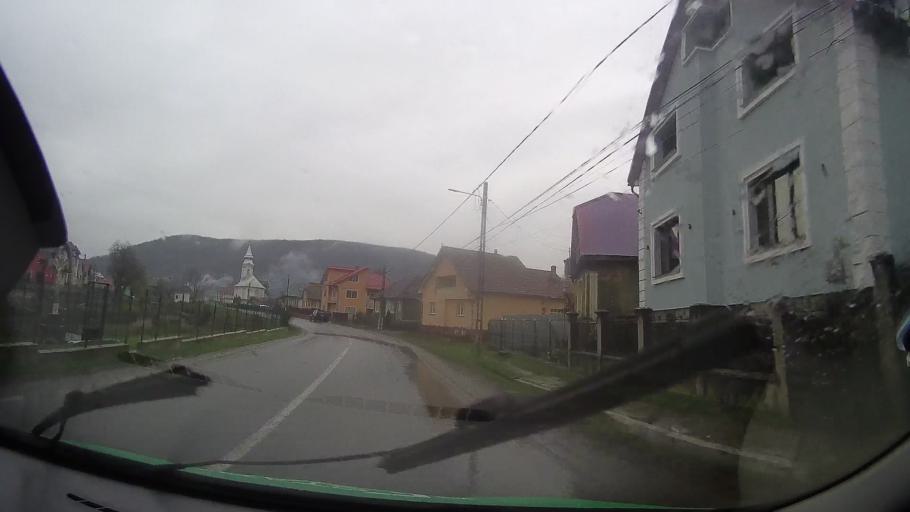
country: RO
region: Bistrita-Nasaud
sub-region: Comuna Sieut
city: Sieut
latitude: 46.9750
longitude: 24.6503
